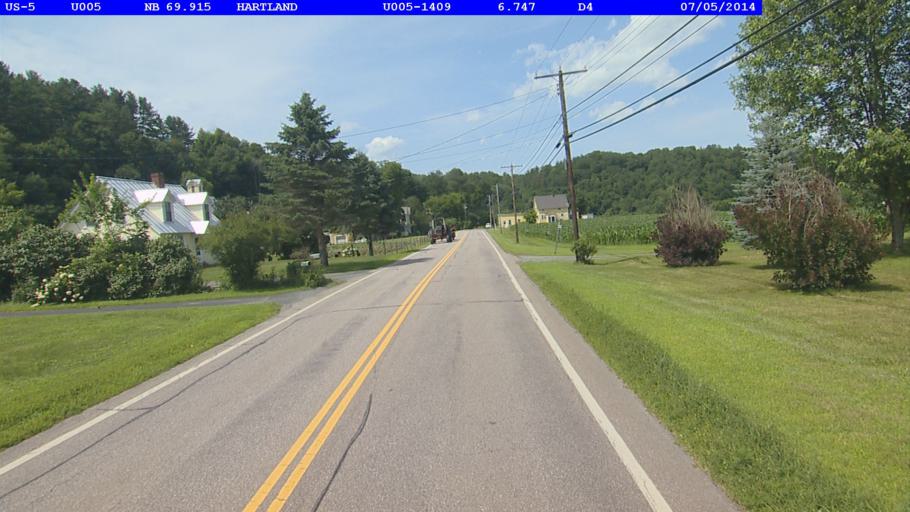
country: US
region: Vermont
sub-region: Windsor County
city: White River Junction
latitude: 43.5978
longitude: -72.3538
